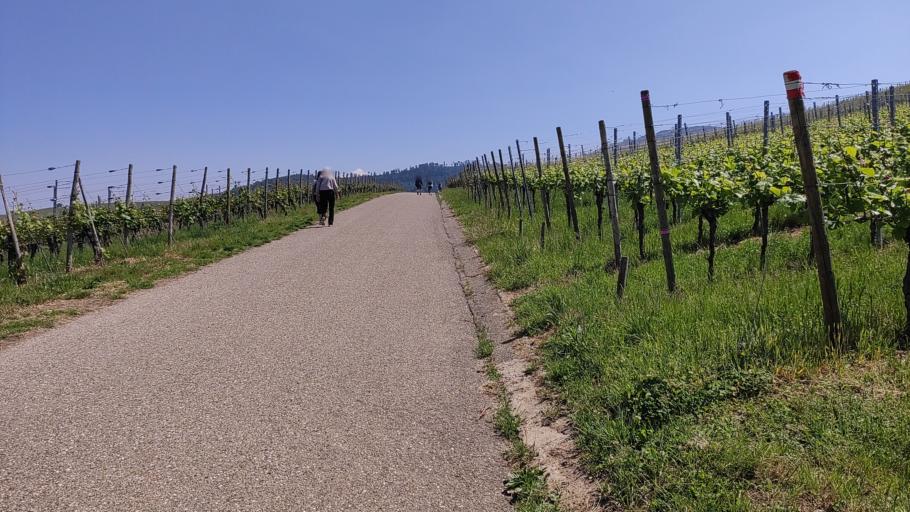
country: DE
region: Baden-Wuerttemberg
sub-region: Freiburg Region
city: Schallstadt
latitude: 47.9527
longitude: 7.7662
